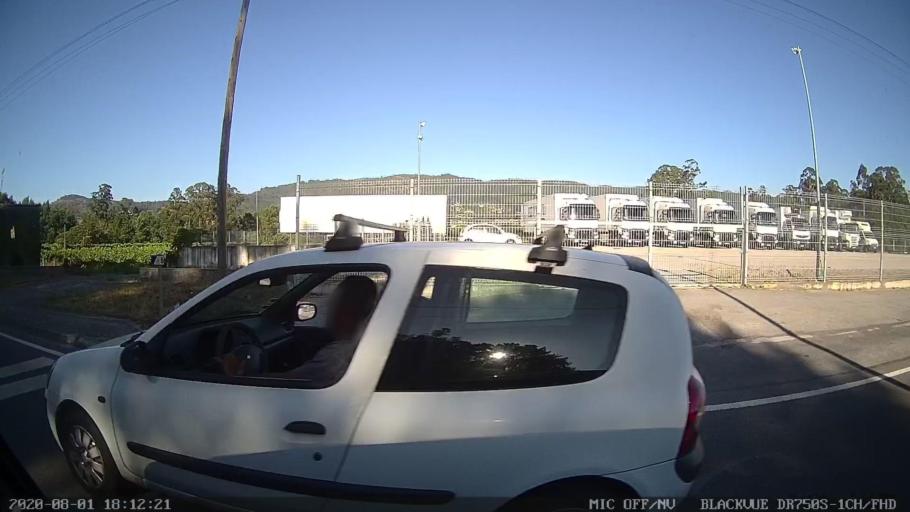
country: PT
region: Porto
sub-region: Santo Tirso
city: Sao Miguel do Couto
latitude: 41.2912
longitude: -8.4711
